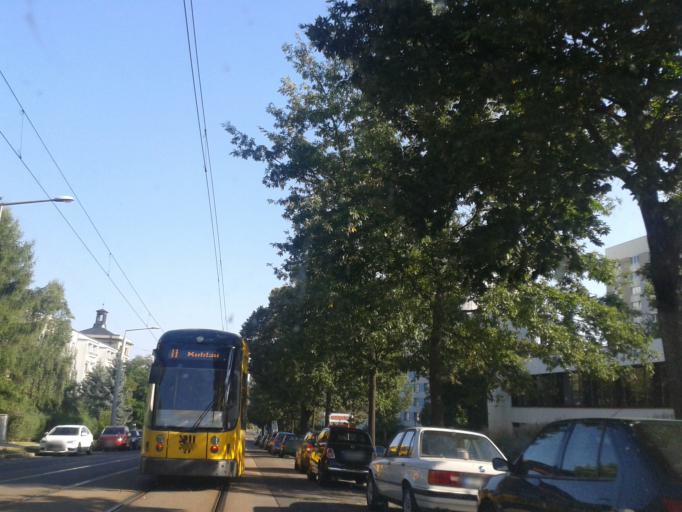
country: DE
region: Saxony
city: Dresden
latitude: 51.0311
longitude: 13.7476
